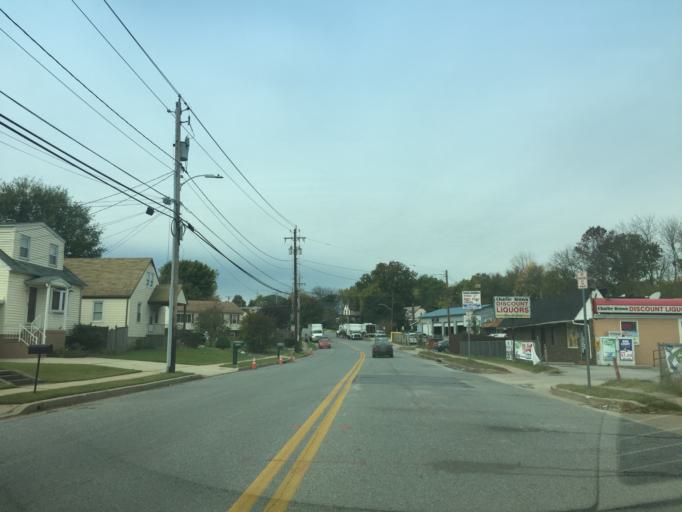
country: US
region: Maryland
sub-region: Baltimore County
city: Overlea
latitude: 39.3416
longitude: -76.5268
